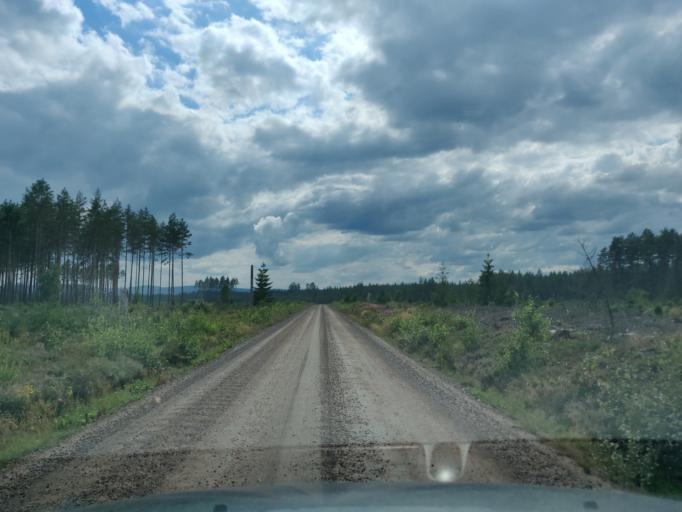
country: SE
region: Vaermland
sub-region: Hagfors Kommun
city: Hagfors
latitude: 59.9835
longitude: 13.5550
